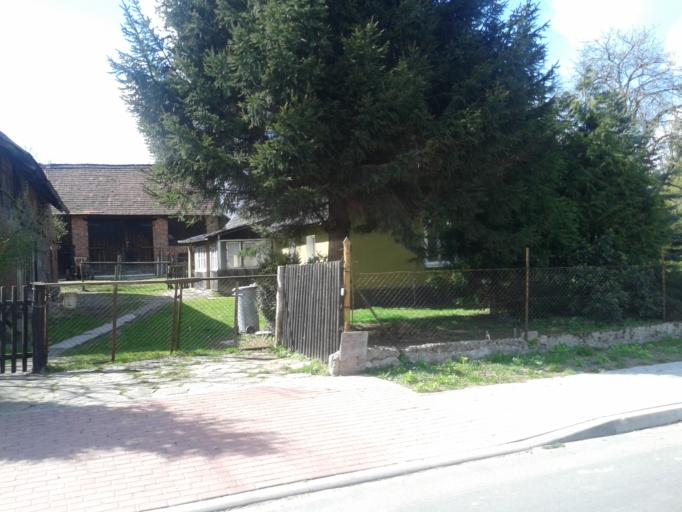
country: PL
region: Lower Silesian Voivodeship
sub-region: Powiat olesnicki
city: Miedzyborz
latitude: 51.4006
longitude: 17.6562
